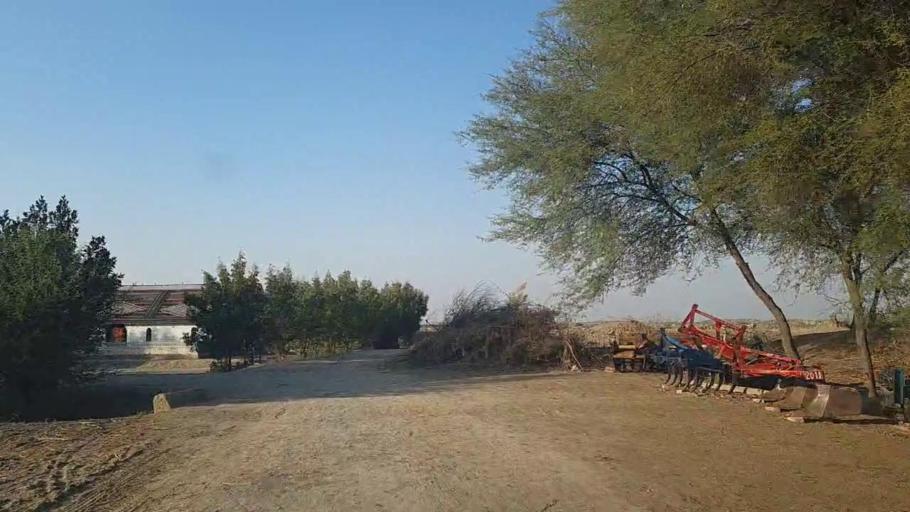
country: PK
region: Sindh
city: Jam Sahib
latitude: 26.3076
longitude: 68.6703
